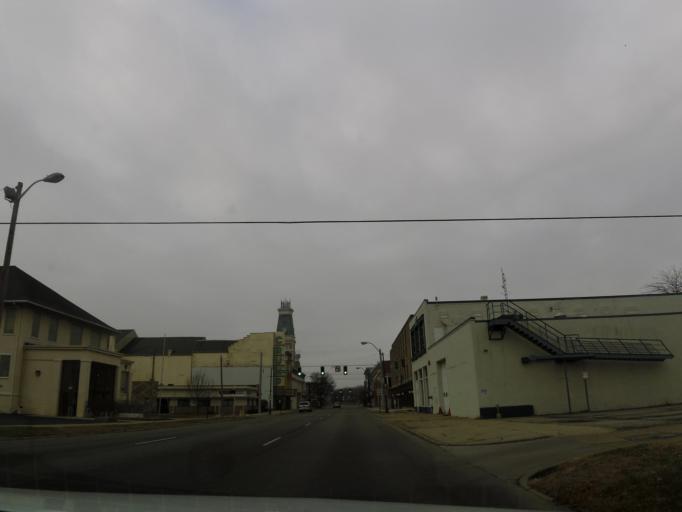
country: US
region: Indiana
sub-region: Bartholomew County
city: Columbus
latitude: 39.2015
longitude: -85.9189
